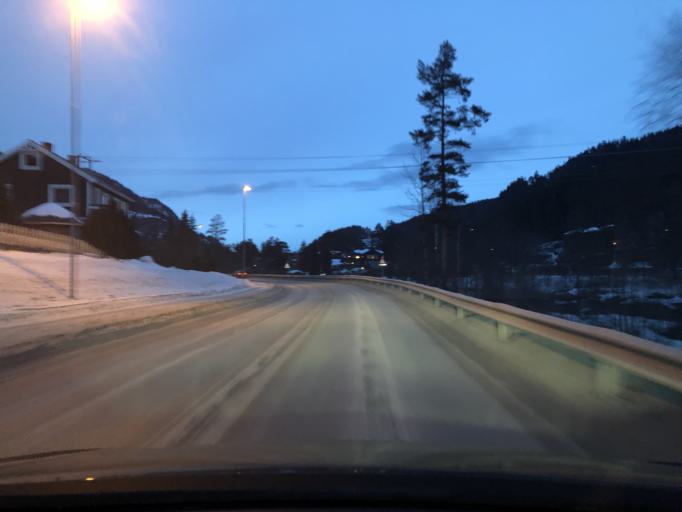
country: NO
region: Oppland
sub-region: Nord-Aurdal
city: Fagernes
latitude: 60.9889
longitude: 9.2251
